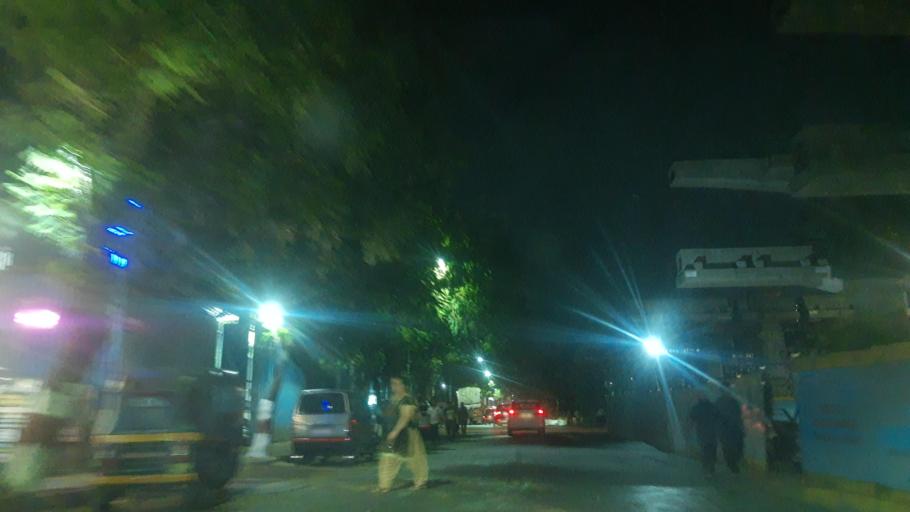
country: IN
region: Maharashtra
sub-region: Thane
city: Thane
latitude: 19.1930
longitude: 72.9625
